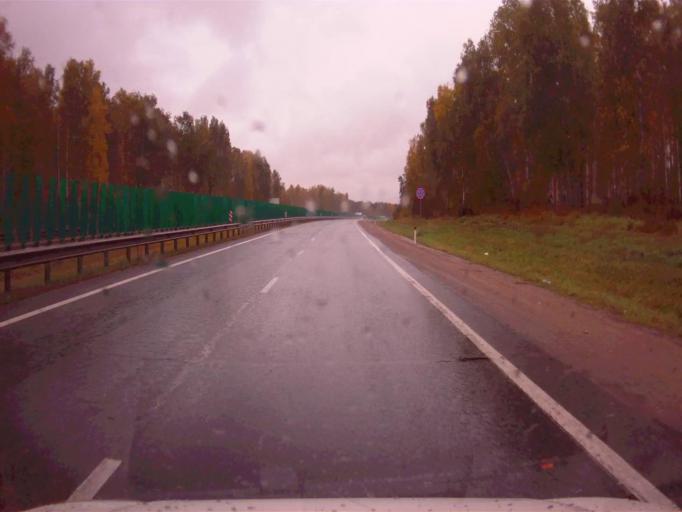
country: RU
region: Chelyabinsk
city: Dolgoderevenskoye
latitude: 55.3347
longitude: 61.3126
